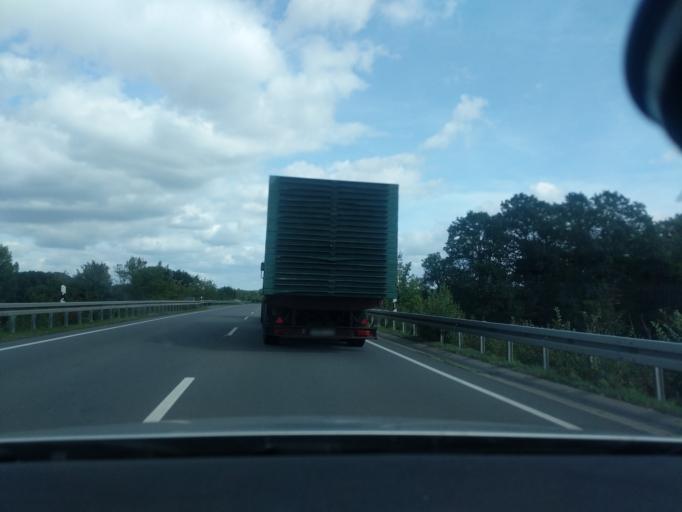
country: DE
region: Lower Saxony
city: Bohmte
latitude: 52.3746
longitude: 8.3040
